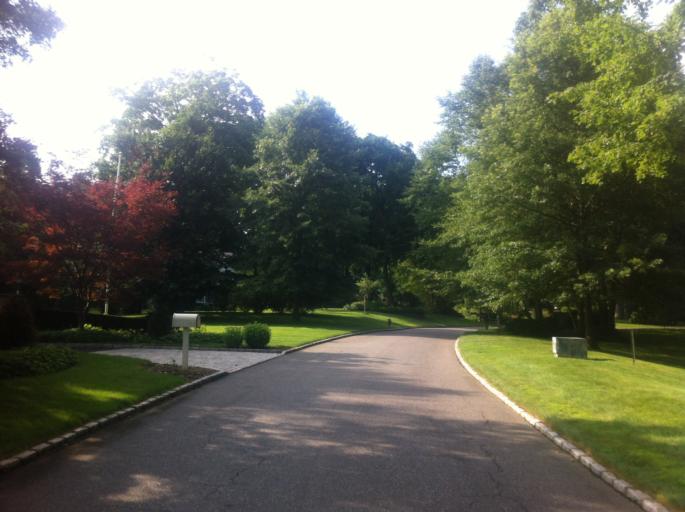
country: US
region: New York
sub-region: Nassau County
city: Old Brookville
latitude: 40.8527
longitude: -73.5969
